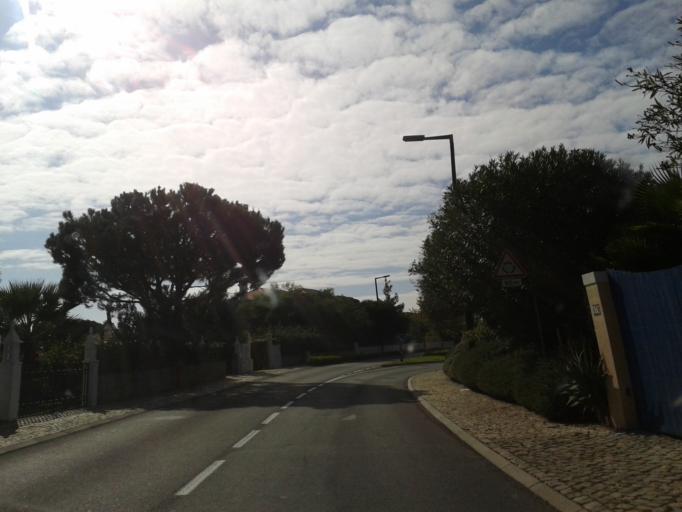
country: PT
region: Faro
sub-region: Loule
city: Almancil
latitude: 37.0574
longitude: -8.0591
